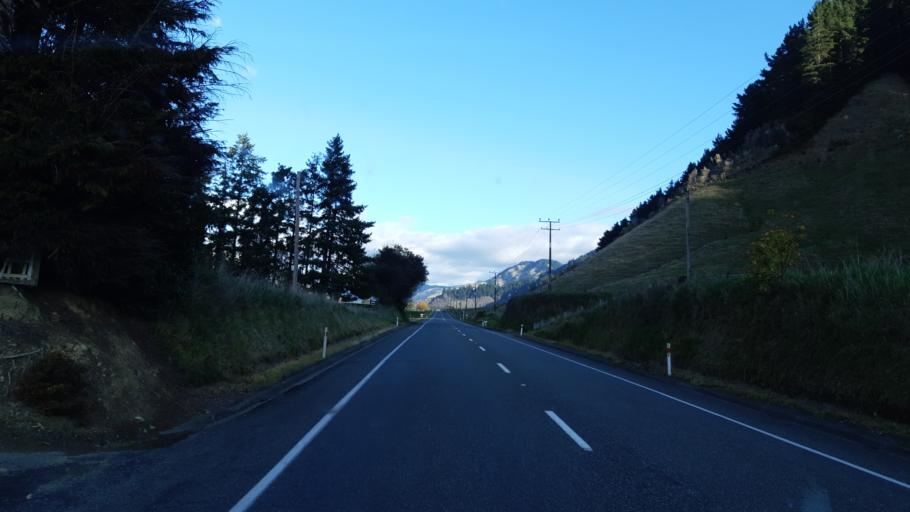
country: NZ
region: Marlborough
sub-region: Marlborough District
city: Picton
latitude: -41.3076
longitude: 173.7674
